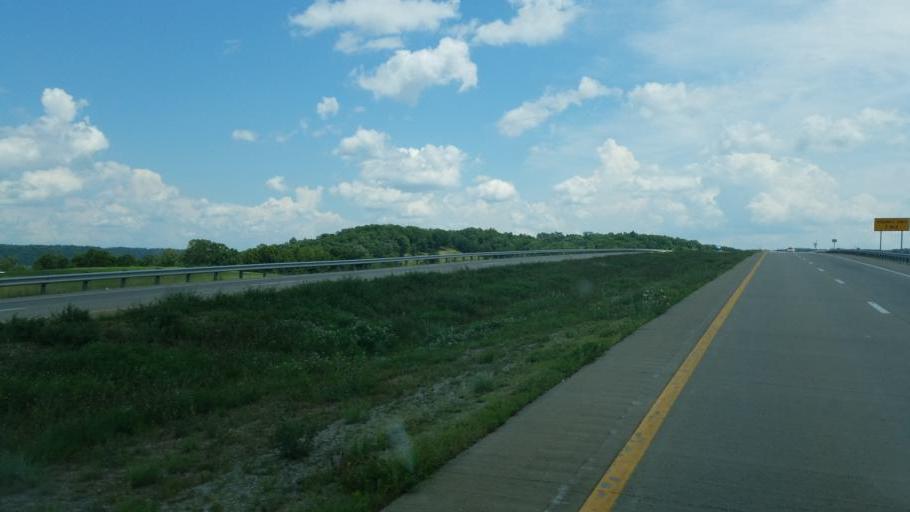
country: US
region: West Virginia
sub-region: Mason County
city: Point Pleasant
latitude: 38.7677
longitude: -82.0297
